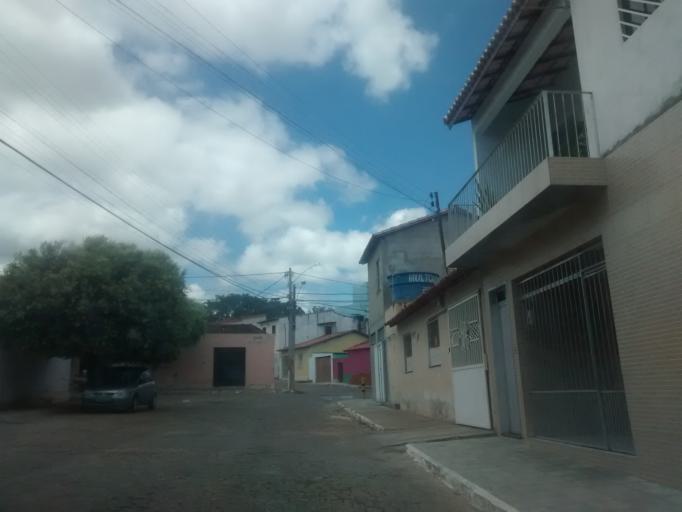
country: BR
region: Bahia
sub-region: Brumado
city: Brumado
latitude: -14.2019
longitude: -41.6732
